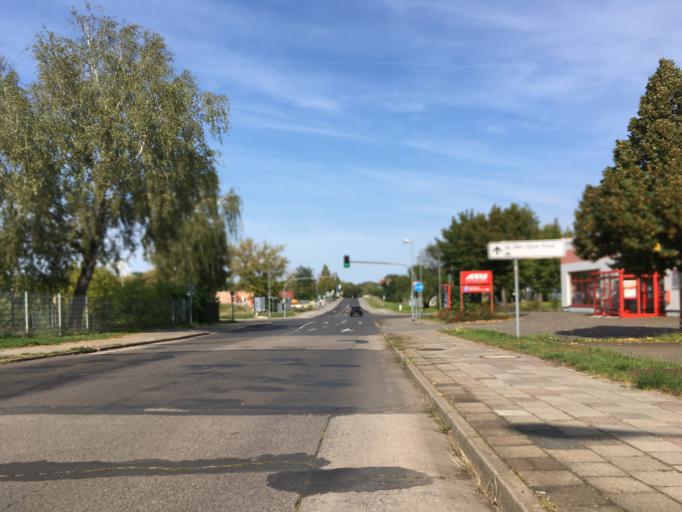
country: DE
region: Brandenburg
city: Eisenhuettenstadt
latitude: 52.1475
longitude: 14.6517
